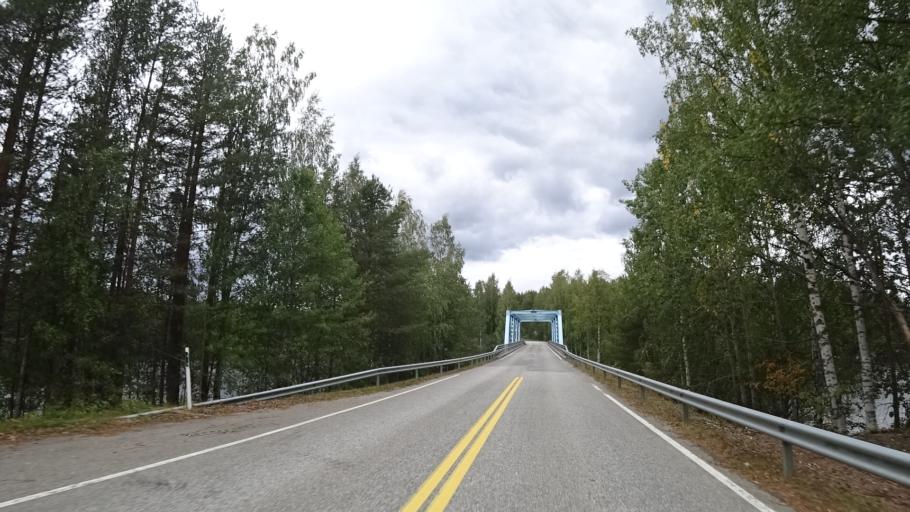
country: FI
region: North Karelia
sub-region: Joensuu
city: Ilomantsi
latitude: 62.6209
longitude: 31.1995
